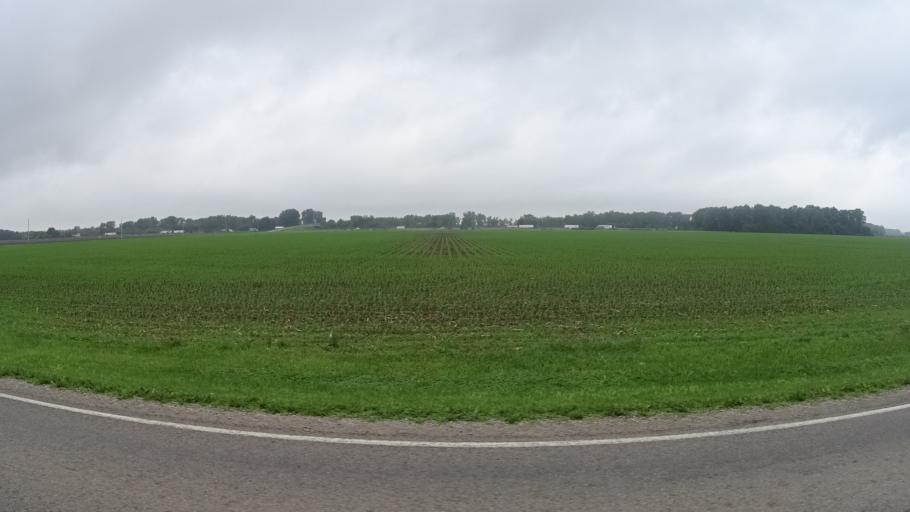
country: US
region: Ohio
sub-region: Huron County
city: Bellevue
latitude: 41.3419
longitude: -82.8148
